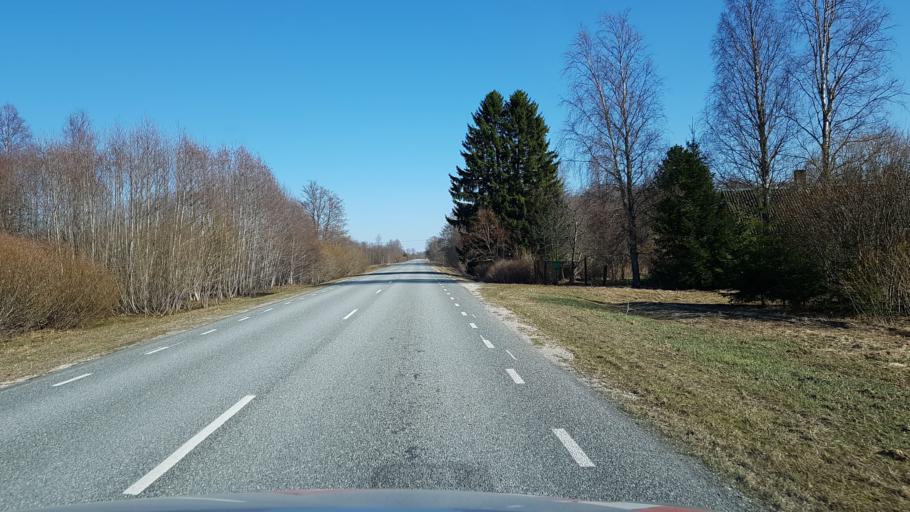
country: EE
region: Laeaene-Virumaa
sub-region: Haljala vald
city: Haljala
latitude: 59.5055
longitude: 26.1177
